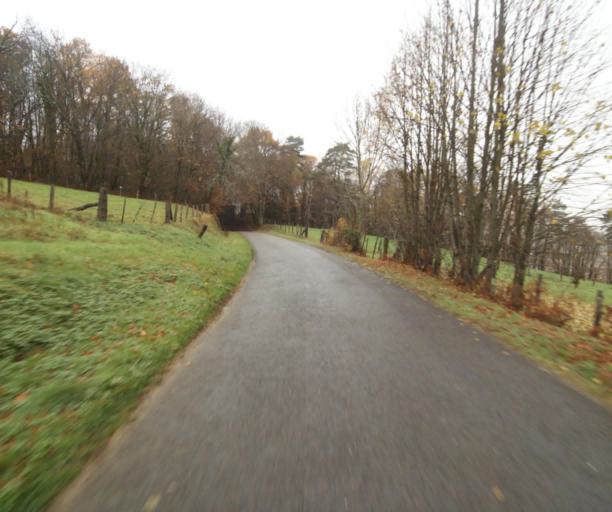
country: FR
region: Limousin
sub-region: Departement de la Correze
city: Cornil
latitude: 45.1977
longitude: 1.6421
